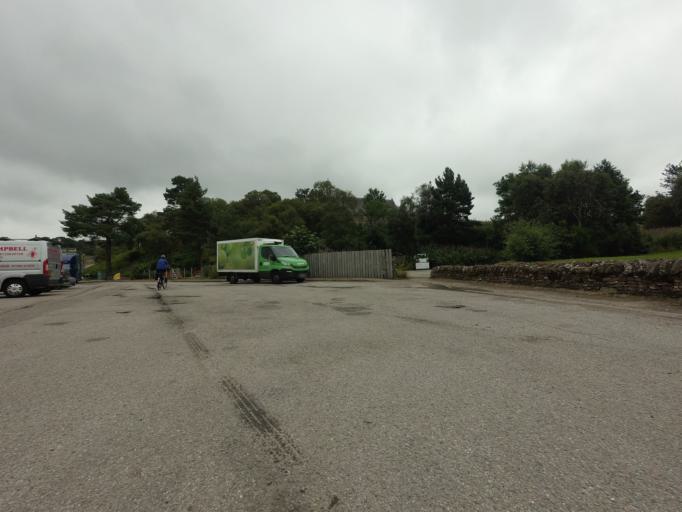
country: GB
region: Scotland
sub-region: Highland
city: Alness
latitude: 58.0247
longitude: -4.4014
